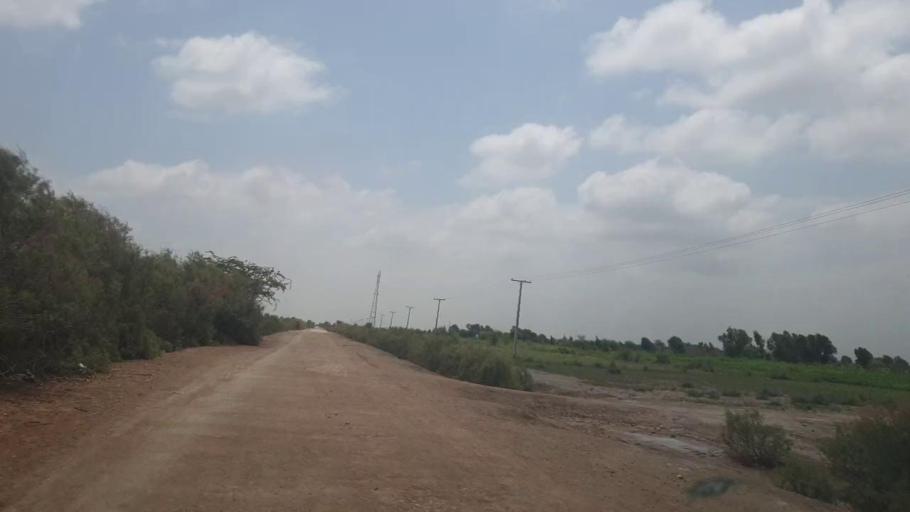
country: PK
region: Sindh
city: Tando Mittha Khan
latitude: 25.9174
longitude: 69.2190
